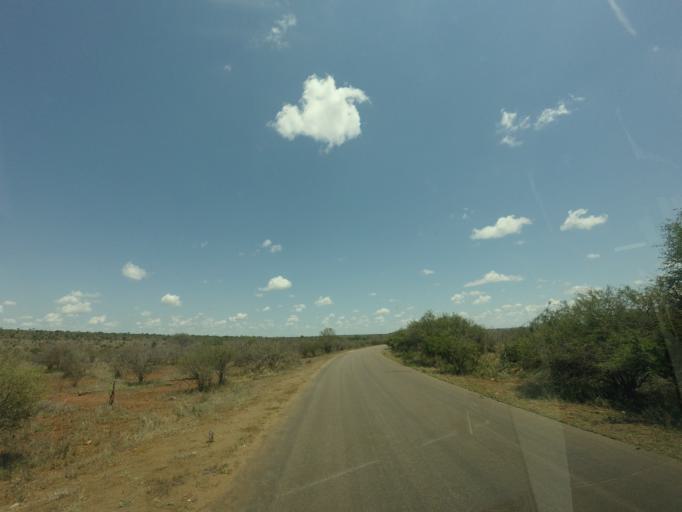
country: ZA
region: Mpumalanga
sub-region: Ehlanzeni District
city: Komatipoort
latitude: -24.8232
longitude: 31.8867
